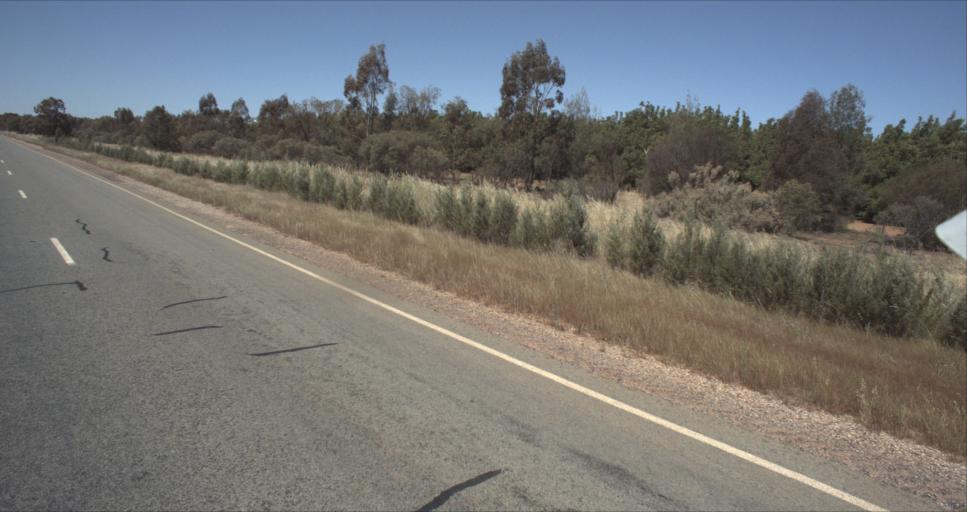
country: AU
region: New South Wales
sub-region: Leeton
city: Leeton
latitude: -34.5000
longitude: 146.4494
